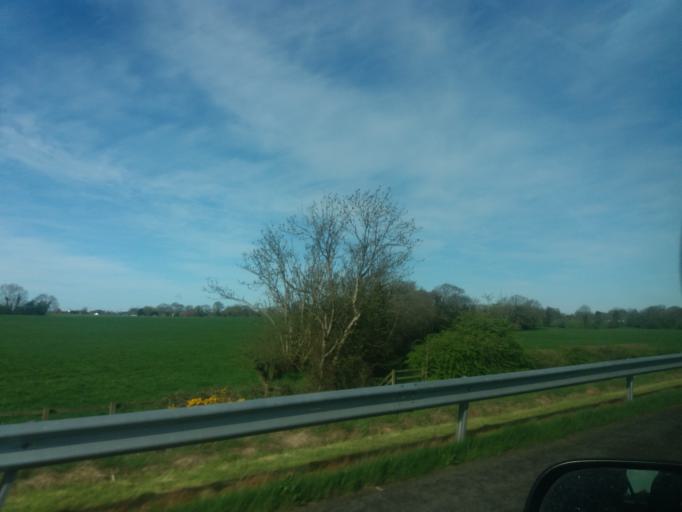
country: IE
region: Leinster
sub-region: An Mhi
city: Kells
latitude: 53.6985
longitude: -6.8353
